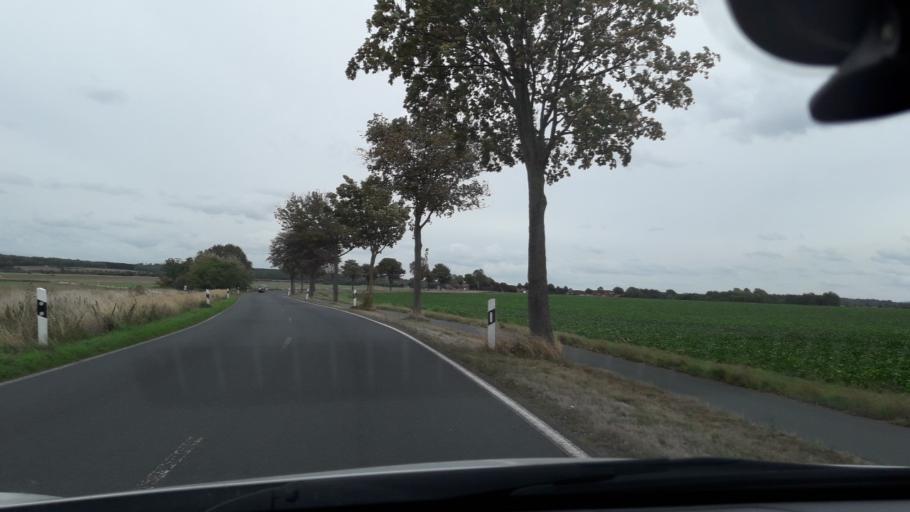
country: DE
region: Lower Saxony
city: Flothe
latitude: 52.0842
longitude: 10.4744
